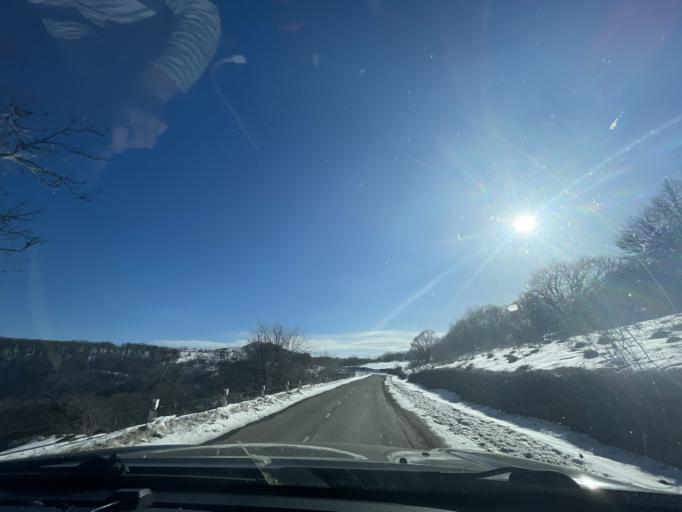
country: GE
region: Kvemo Kartli
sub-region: Tetri Tsqaro
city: Manglisi
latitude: 41.7668
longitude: 44.5070
